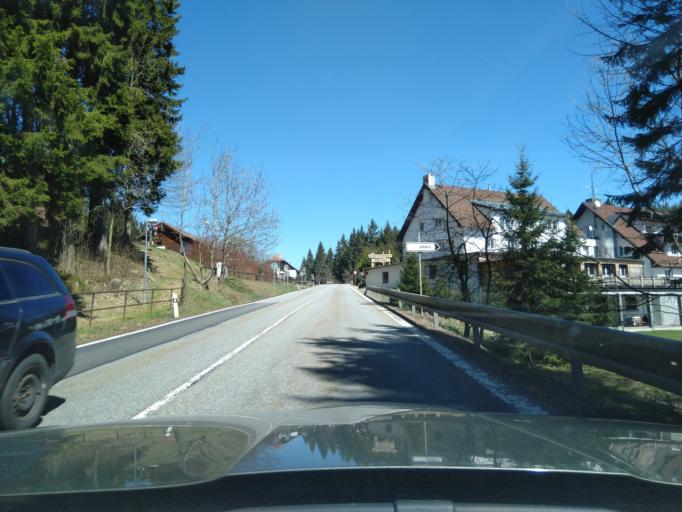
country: CZ
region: Jihocesky
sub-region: Okres Prachatice
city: Vimperk
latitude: 48.9826
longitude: 13.7714
